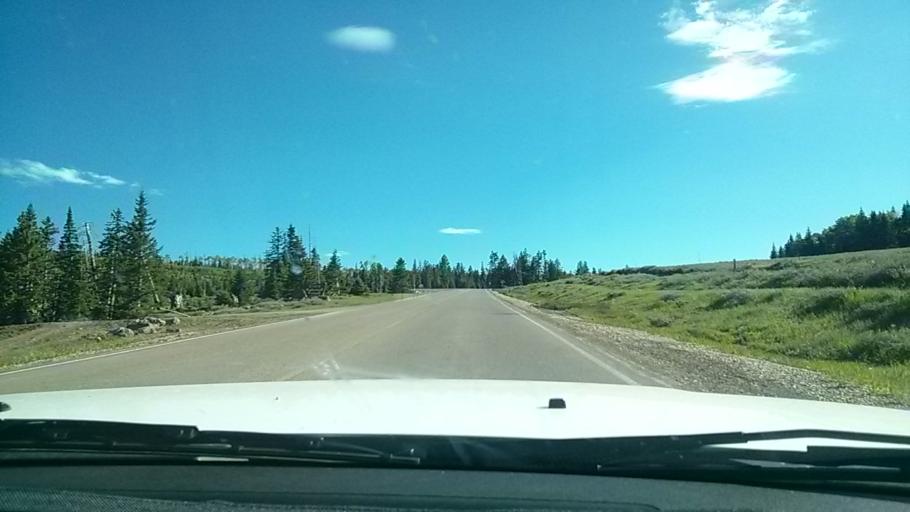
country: US
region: Utah
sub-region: Iron County
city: Parowan
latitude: 37.6850
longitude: -112.8539
